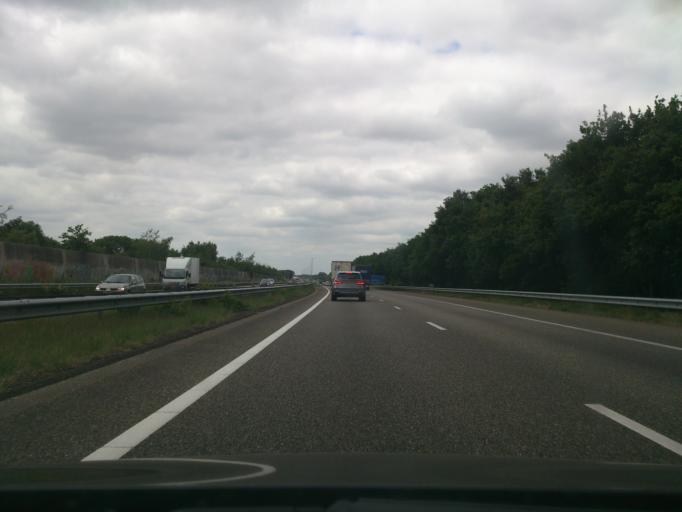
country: NL
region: North Brabant
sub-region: Gemeente Bernheze
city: Heesch
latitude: 51.7398
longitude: 5.5256
